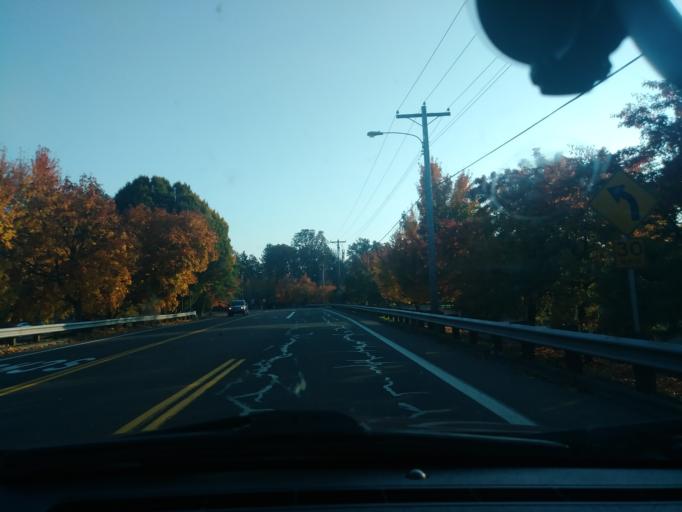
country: US
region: Oregon
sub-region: Washington County
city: Forest Grove
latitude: 45.5215
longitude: -123.1216
